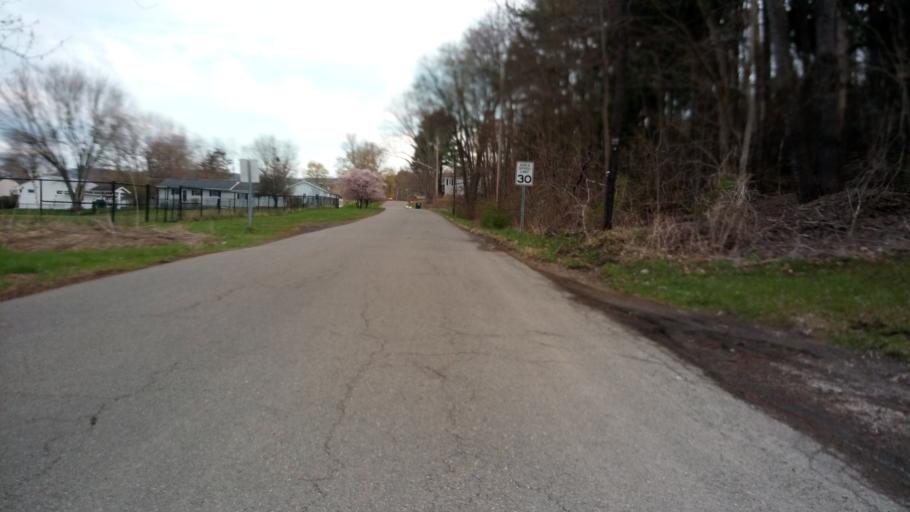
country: US
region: New York
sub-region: Chemung County
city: Southport
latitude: 42.0699
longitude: -76.8225
